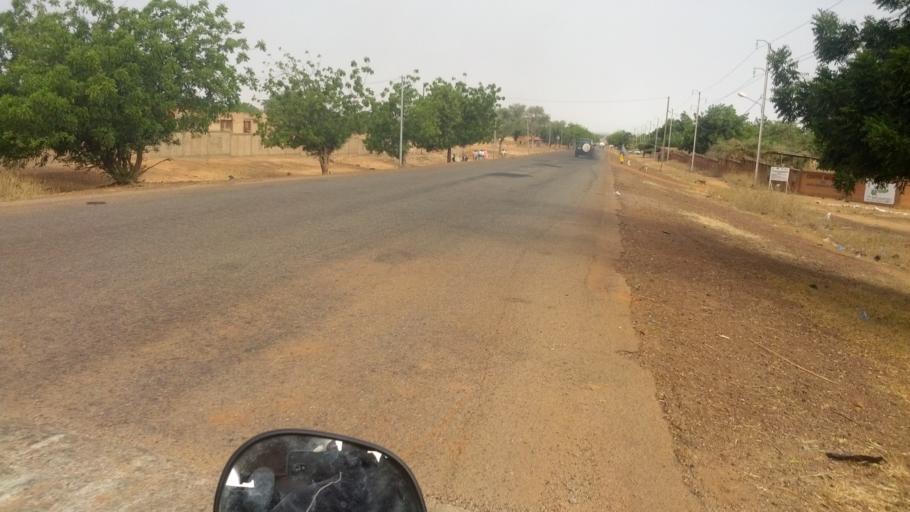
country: BF
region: Centre-Nord
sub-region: Province du Sanmatenga
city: Kaya
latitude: 12.9035
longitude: -1.0784
